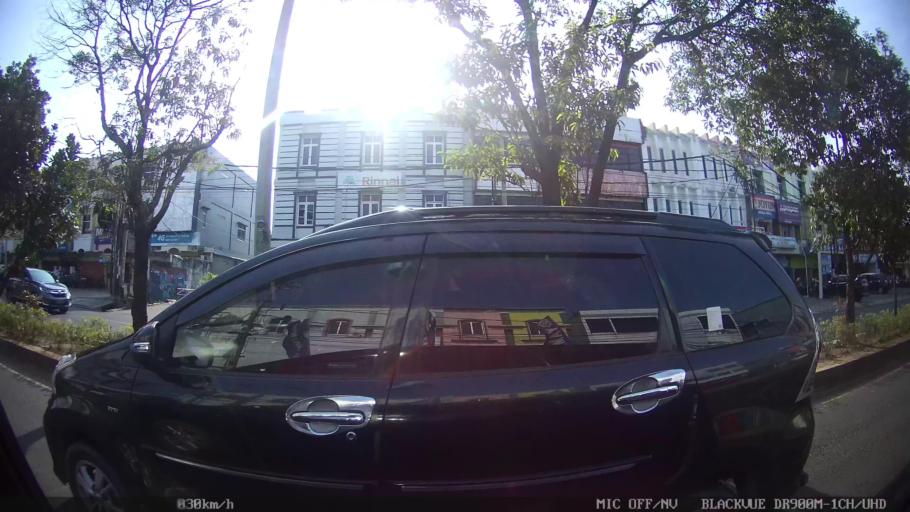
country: ID
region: Lampung
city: Kedaton
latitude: -5.3961
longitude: 105.2617
